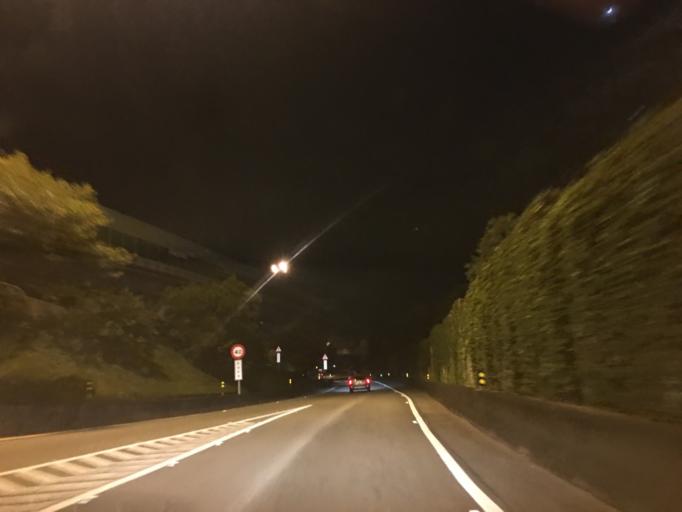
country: TW
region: Taiwan
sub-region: Hsinchu
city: Hsinchu
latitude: 24.7904
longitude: 121.0049
